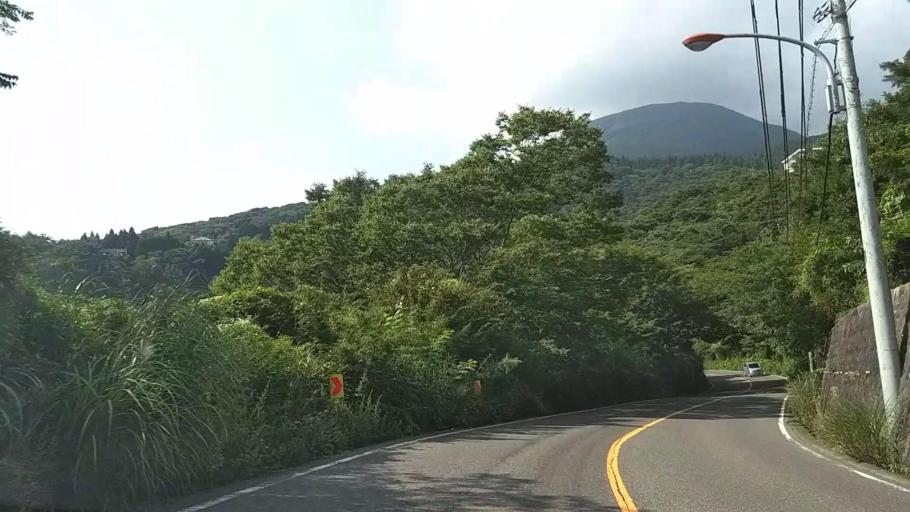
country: JP
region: Kanagawa
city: Hakone
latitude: 35.2070
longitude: 139.0318
